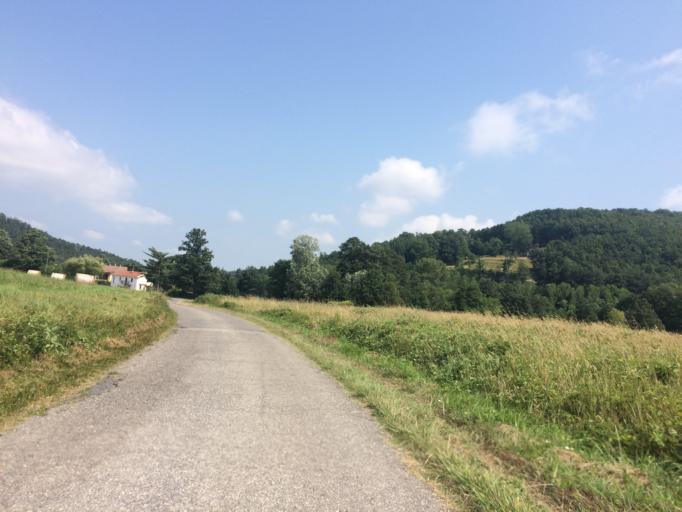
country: IT
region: Liguria
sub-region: Provincia di Savona
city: Piana Crixia
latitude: 44.4725
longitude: 8.3517
